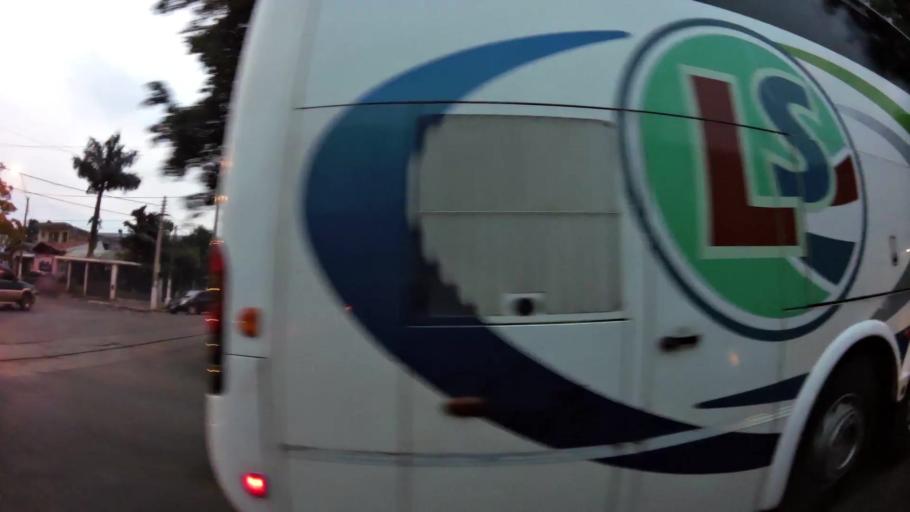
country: PY
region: Central
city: Lambare
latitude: -25.3288
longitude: -57.5995
